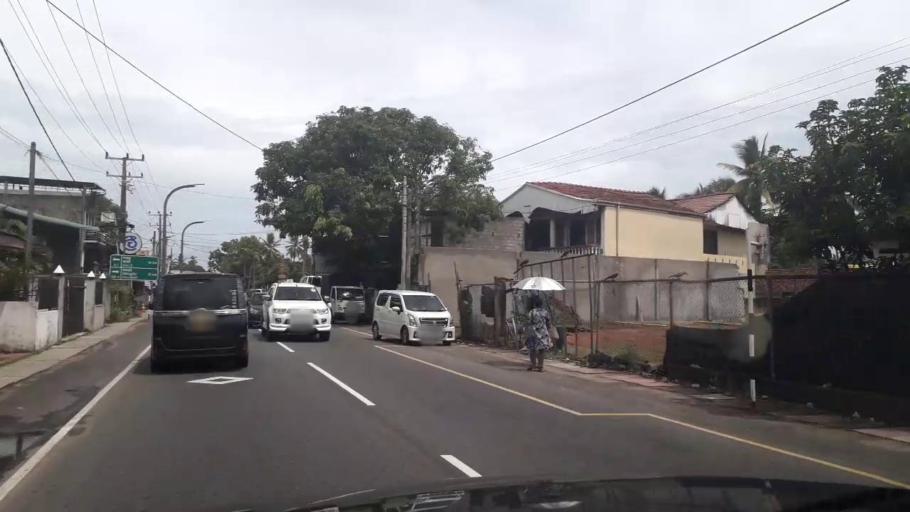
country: LK
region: Western
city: Panadura
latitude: 6.7279
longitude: 79.9053
